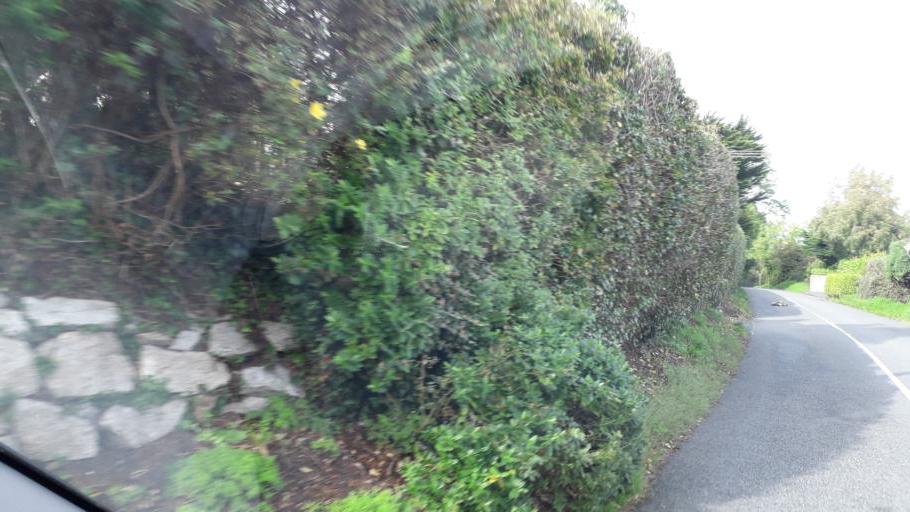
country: IE
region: Leinster
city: Sandyford
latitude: 53.2477
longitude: -6.2166
